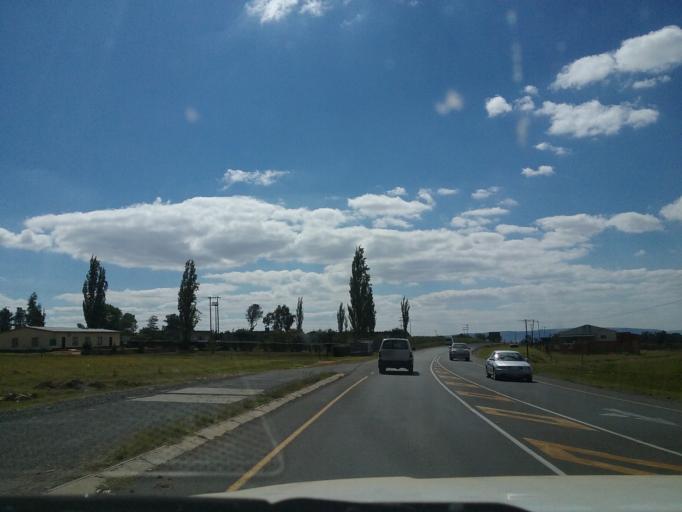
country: LS
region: Maseru
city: Maseru
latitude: -29.4840
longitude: 27.5266
